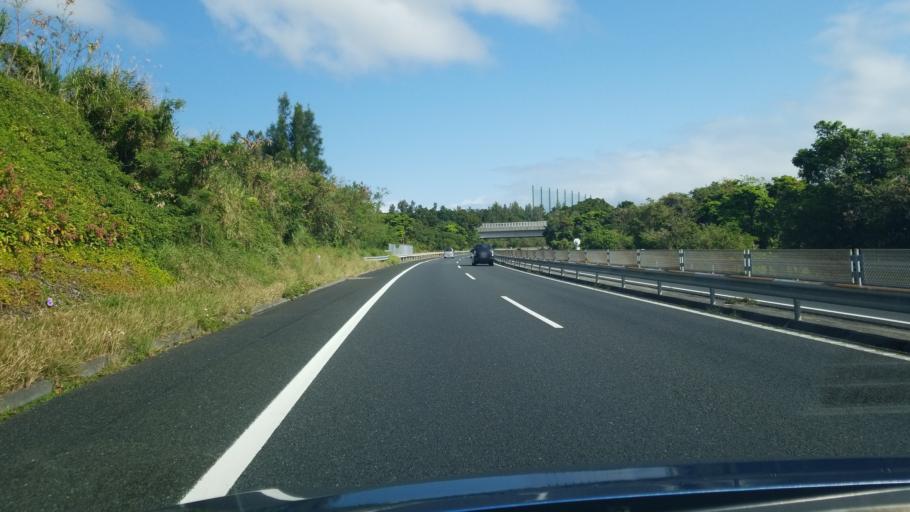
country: JP
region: Okinawa
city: Ishikawa
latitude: 26.3818
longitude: 127.8194
